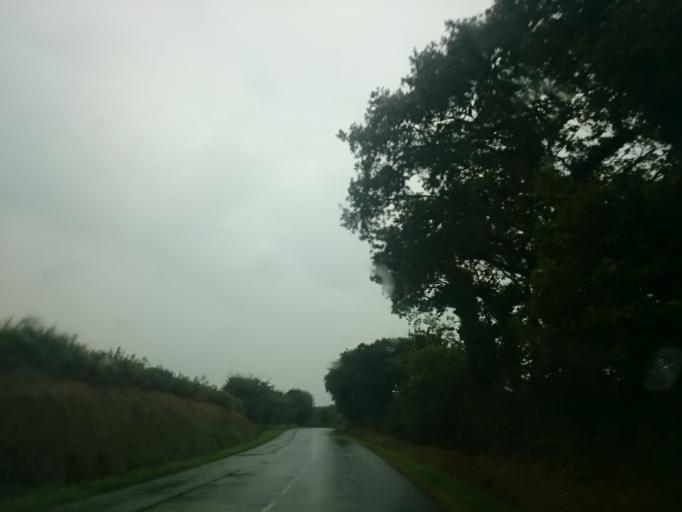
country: FR
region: Brittany
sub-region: Departement du Finistere
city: Plouvien
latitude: 48.5338
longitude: -4.4360
